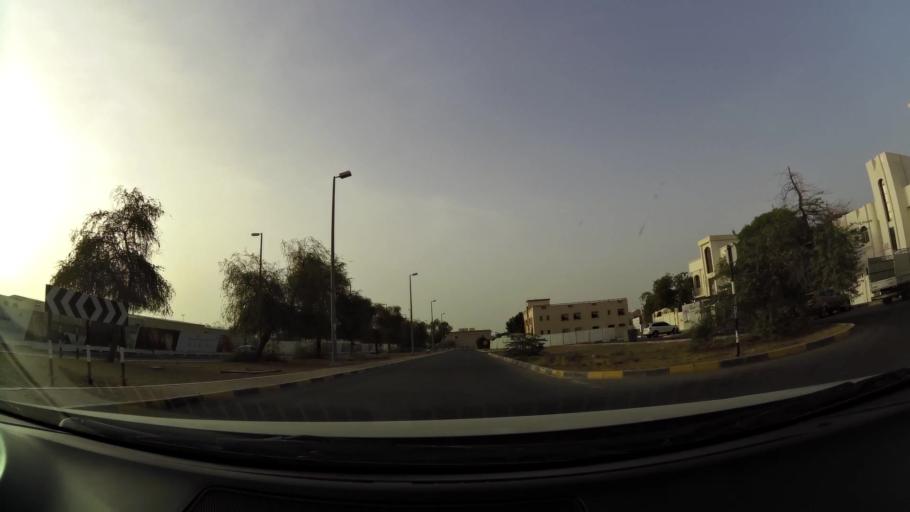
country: AE
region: Abu Dhabi
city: Al Ain
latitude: 24.2459
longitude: 55.7287
